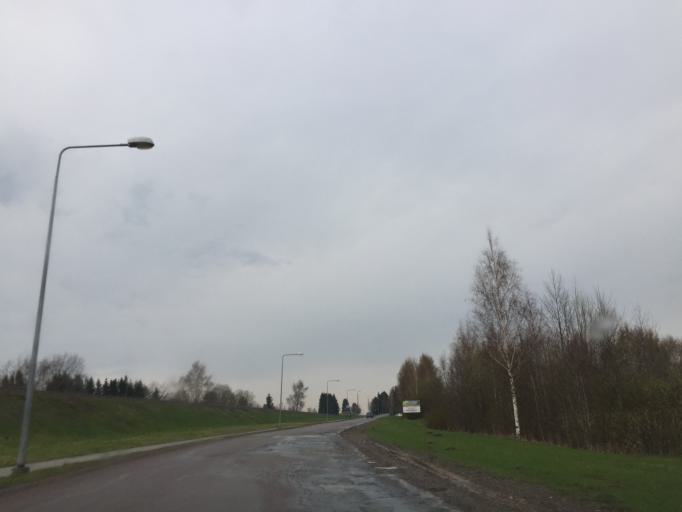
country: EE
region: Tartu
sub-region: UElenurme vald
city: Ulenurme
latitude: 58.3066
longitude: 26.7230
